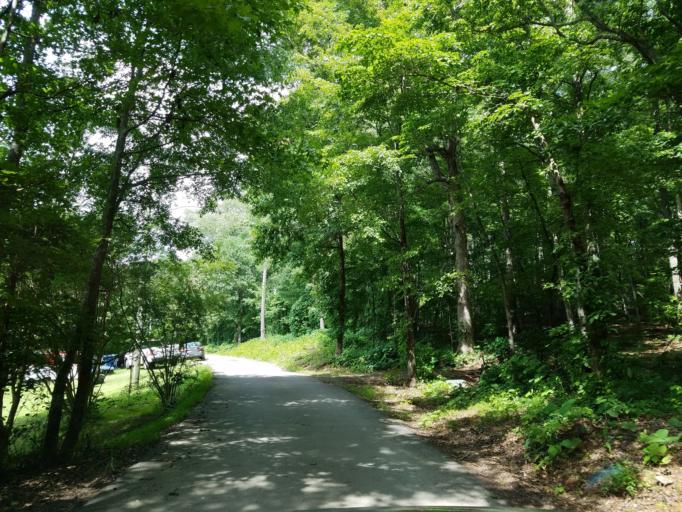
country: US
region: Georgia
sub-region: Cherokee County
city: Ball Ground
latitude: 34.3300
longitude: -84.3821
